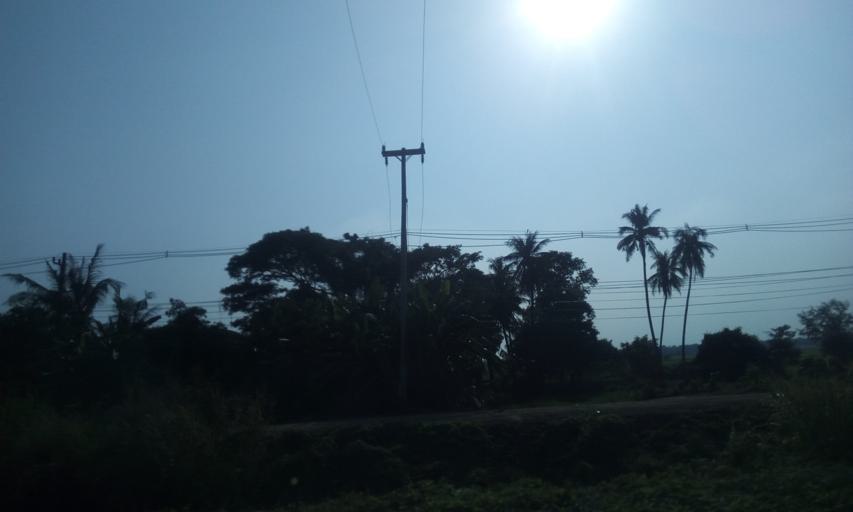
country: TH
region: Sing Buri
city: Sing Buri
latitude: 14.8412
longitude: 100.4325
